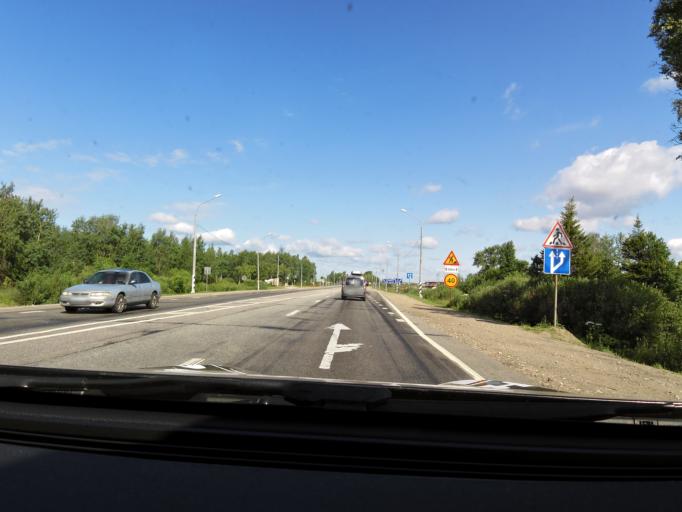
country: RU
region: Tverskaya
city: Tver
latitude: 56.8059
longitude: 35.8450
